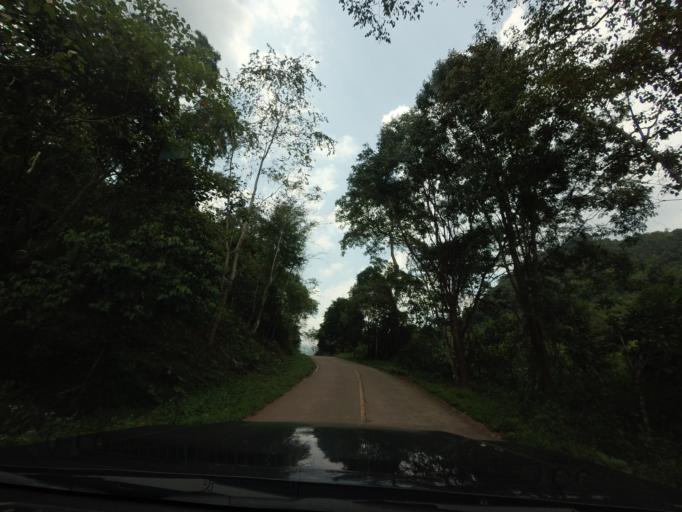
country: TH
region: Nan
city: Bo Kluea
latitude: 19.1943
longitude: 101.1945
